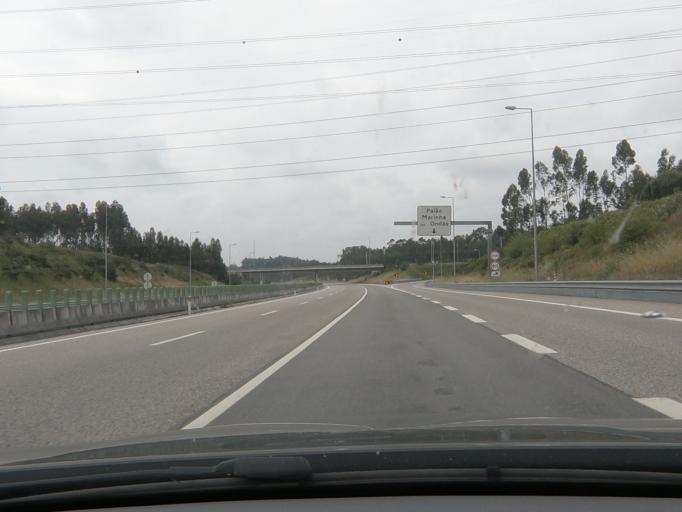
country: PT
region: Coimbra
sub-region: Figueira da Foz
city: Lavos
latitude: 40.0464
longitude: -8.8114
